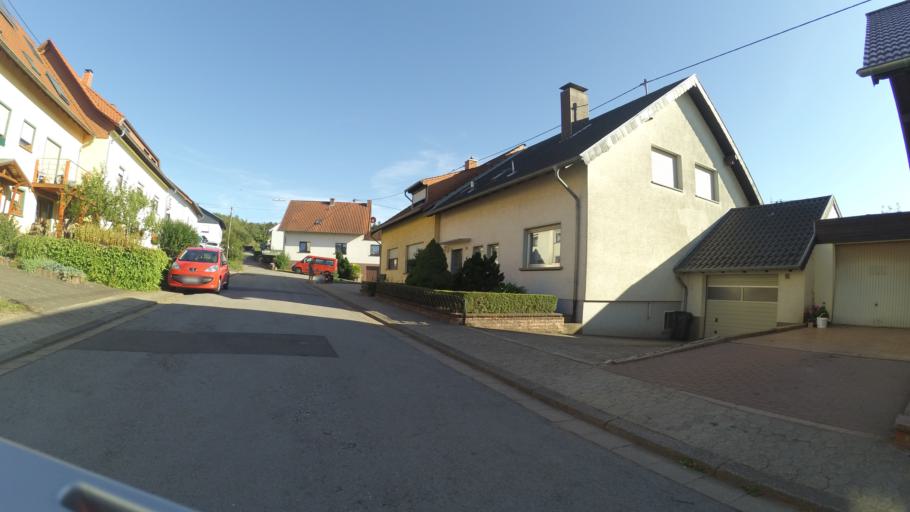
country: DE
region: Saarland
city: Eppelborn
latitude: 49.4311
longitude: 6.9550
